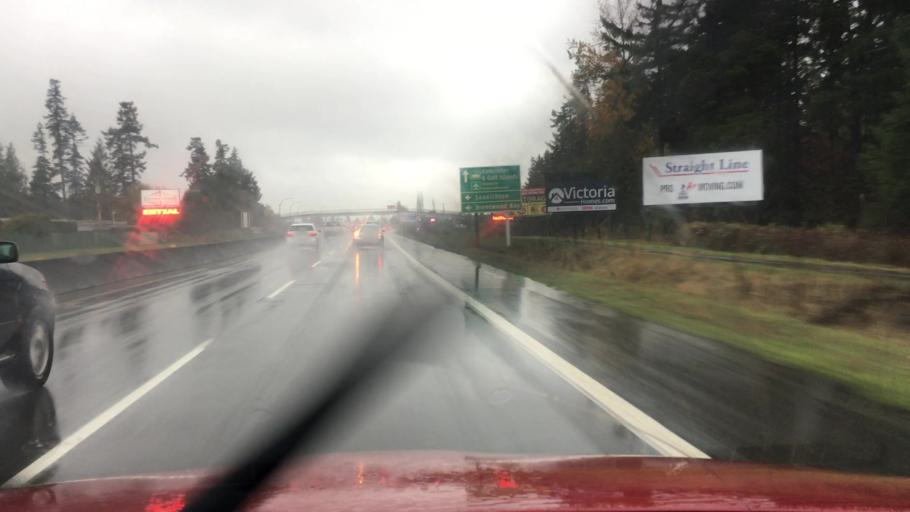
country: CA
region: British Columbia
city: North Saanich
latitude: 48.5905
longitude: -123.3999
